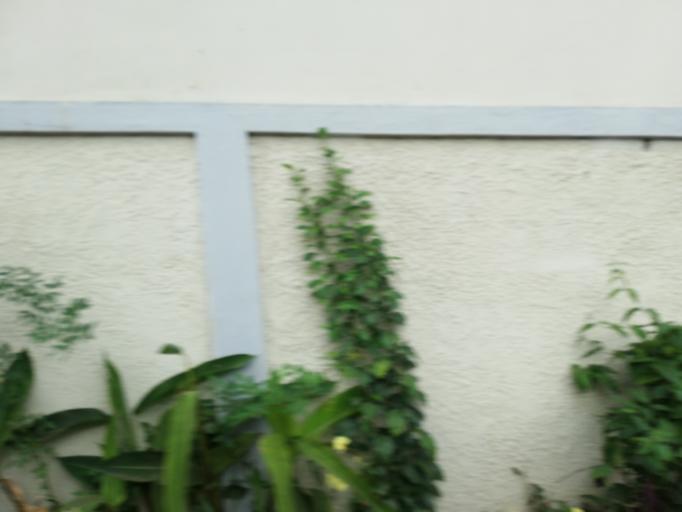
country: MU
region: Black River
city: Gros Cailloux
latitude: -20.2289
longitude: 57.4528
